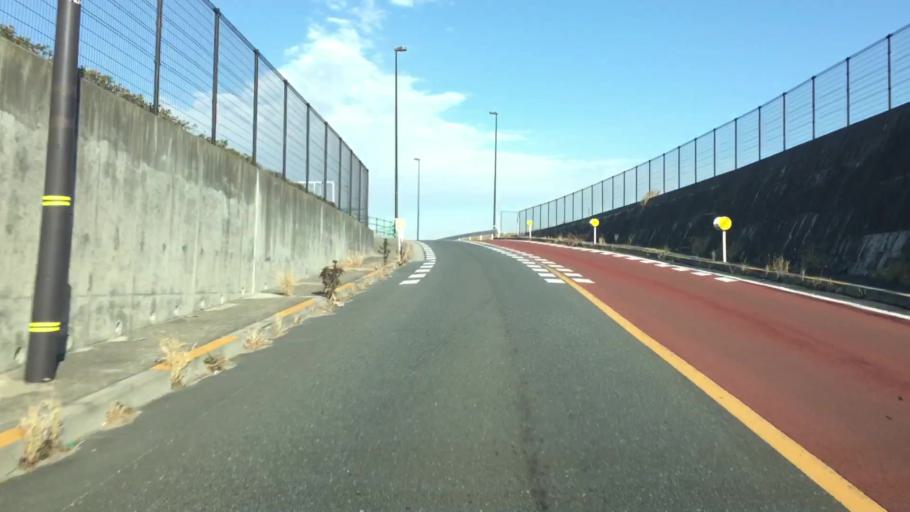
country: JP
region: Saitama
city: Kawaguchi
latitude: 35.7665
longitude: 139.7565
